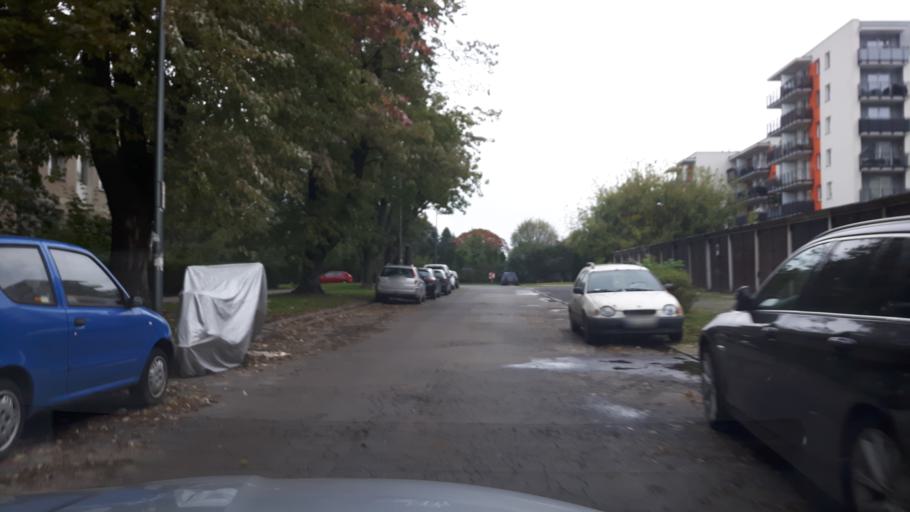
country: PL
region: Masovian Voivodeship
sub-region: Warszawa
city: Praga Poludnie
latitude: 52.2497
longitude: 21.0987
